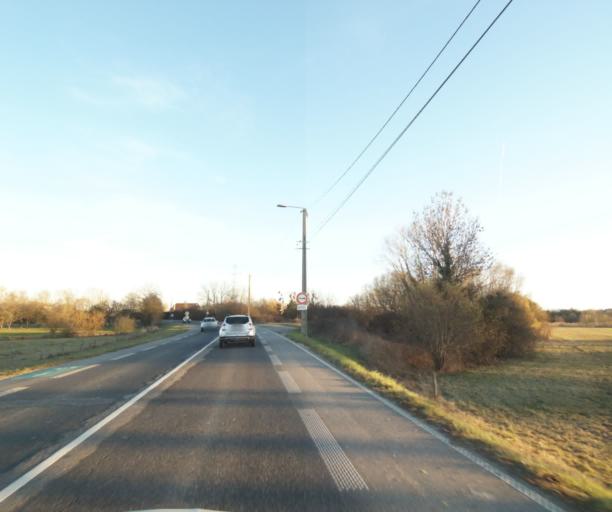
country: FR
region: Lorraine
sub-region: Departement de Meurthe-et-Moselle
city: Laneuveville-devant-Nancy
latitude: 48.6628
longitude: 6.2380
